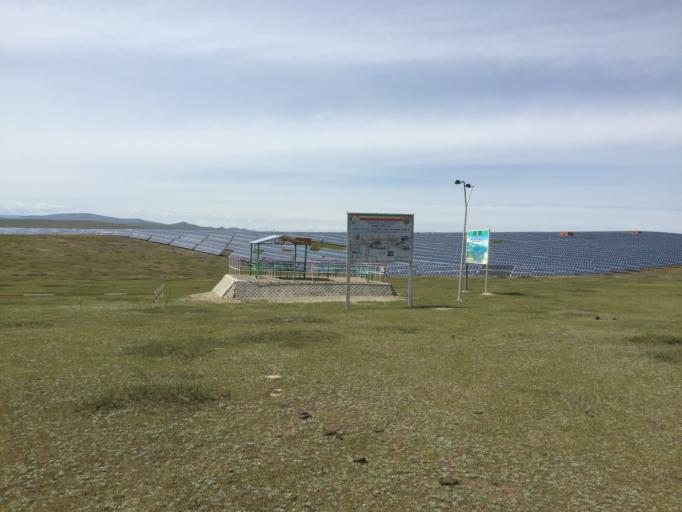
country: MN
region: Darhan Uul
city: Darhan
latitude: 49.3968
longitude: 105.9451
